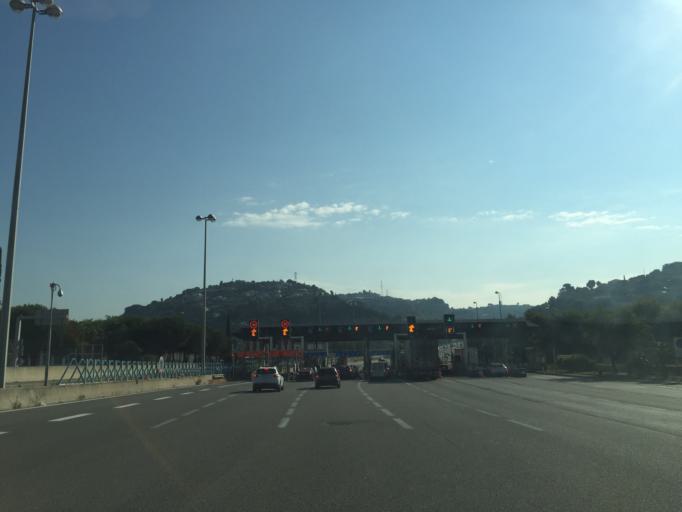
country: FR
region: Provence-Alpes-Cote d'Azur
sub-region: Departement des Alpes-Maritimes
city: Saint-Laurent-du-Var
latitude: 43.7070
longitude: 7.1906
